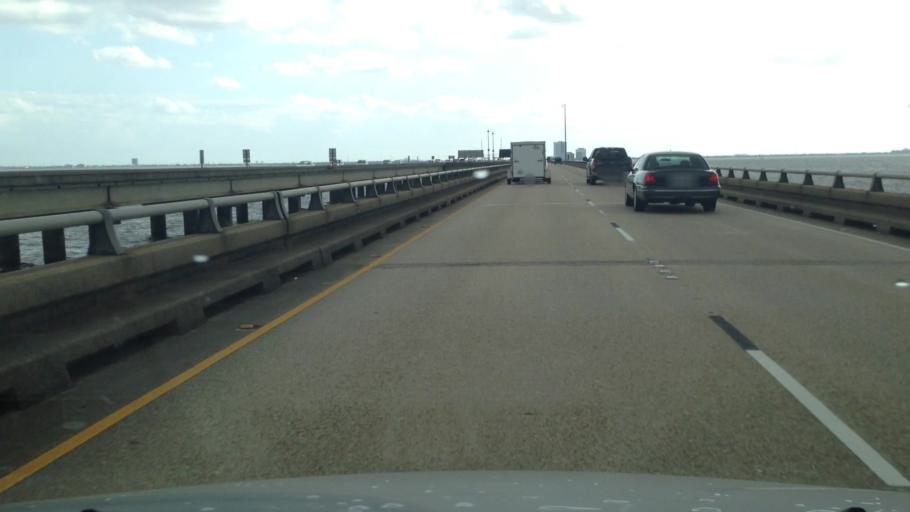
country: US
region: Louisiana
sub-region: Jefferson Parish
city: Metairie
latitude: 30.0729
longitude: -90.1451
